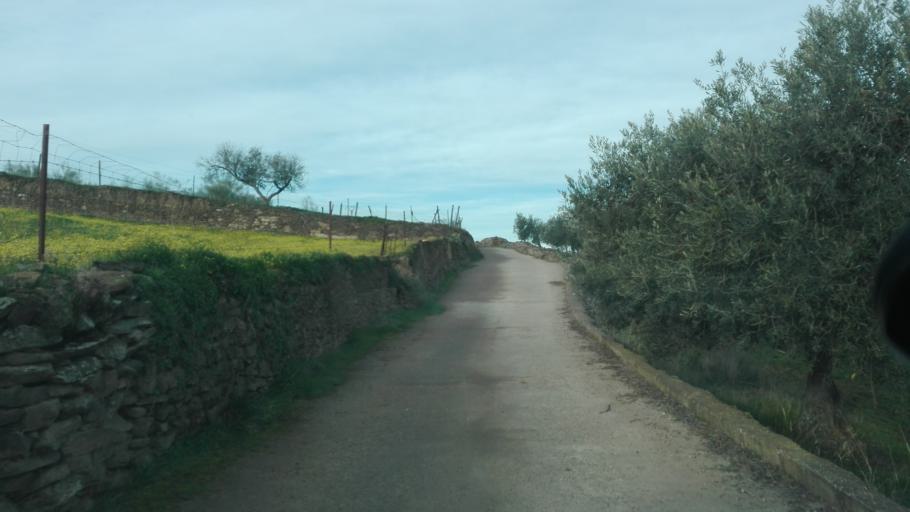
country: ES
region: Extremadura
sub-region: Provincia de Badajoz
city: Llera
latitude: 38.4496
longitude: -6.0587
